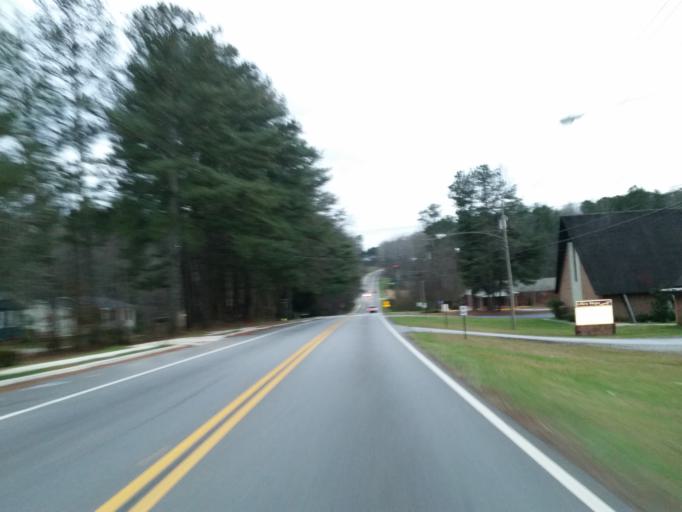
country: US
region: Georgia
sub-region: Cobb County
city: Mableton
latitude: 33.8719
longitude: -84.5789
